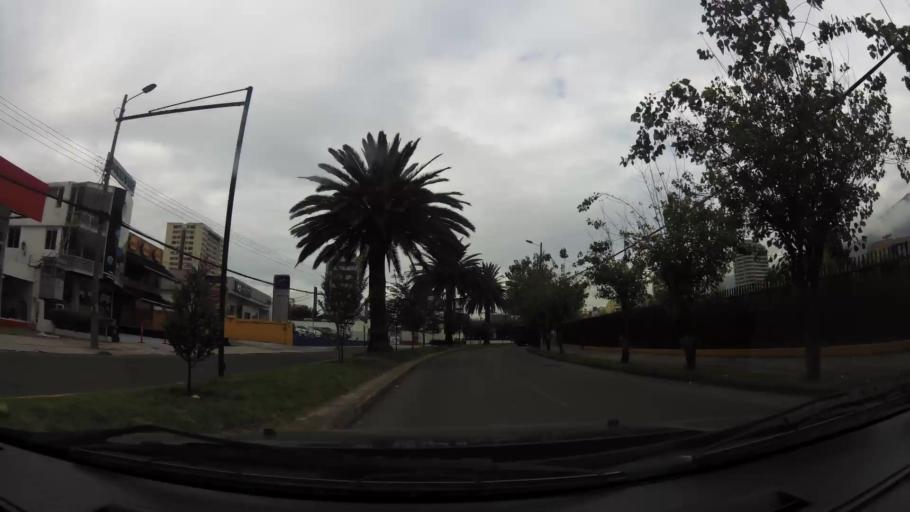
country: EC
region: Pichincha
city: Quito
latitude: -0.1971
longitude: -78.4853
